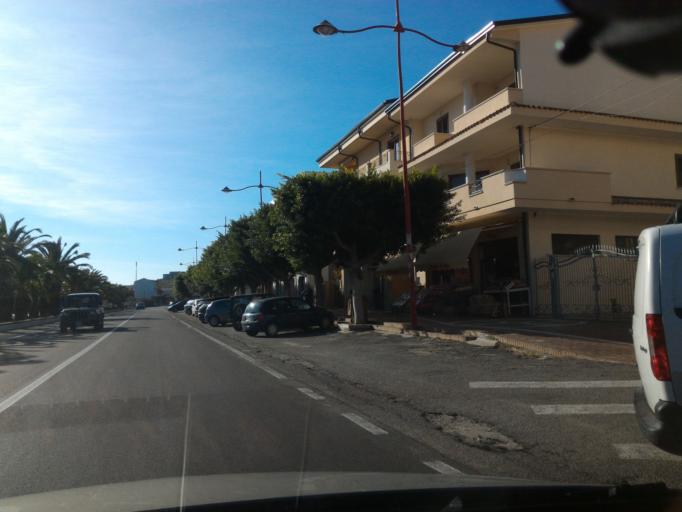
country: IT
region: Calabria
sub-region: Provincia di Crotone
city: Torre Melissa
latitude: 39.3085
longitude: 17.1082
